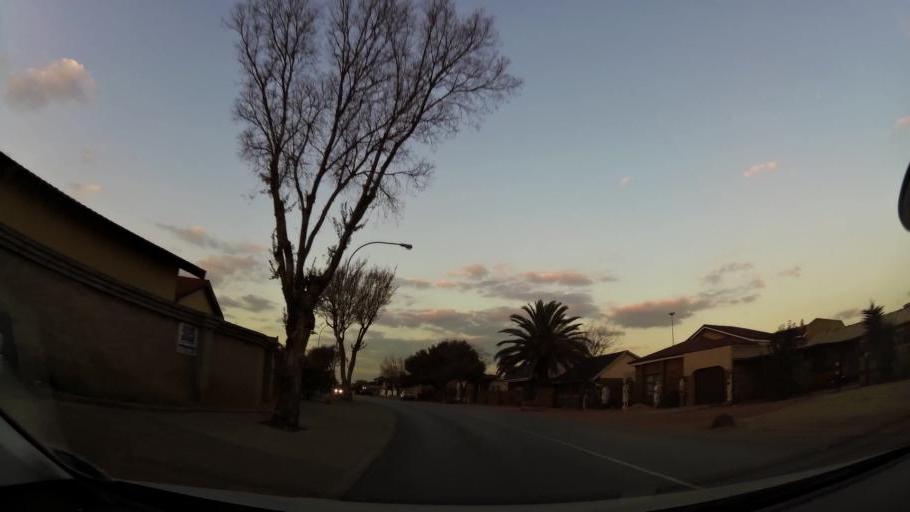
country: ZA
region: Gauteng
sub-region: City of Johannesburg Metropolitan Municipality
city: Soweto
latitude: -26.2729
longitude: 27.9028
